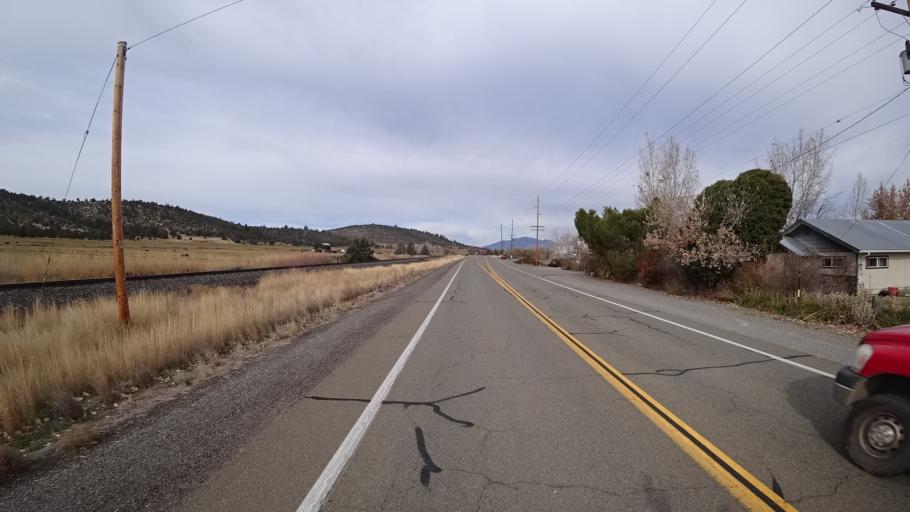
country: US
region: California
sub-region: Siskiyou County
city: Montague
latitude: 41.6825
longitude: -122.5319
